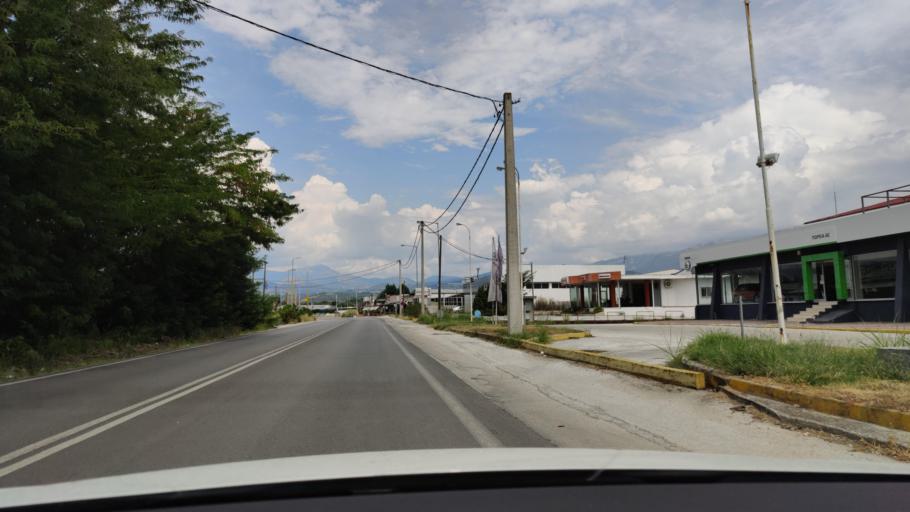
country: GR
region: Central Macedonia
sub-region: Nomos Serron
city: Serres
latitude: 41.0628
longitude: 23.5396
